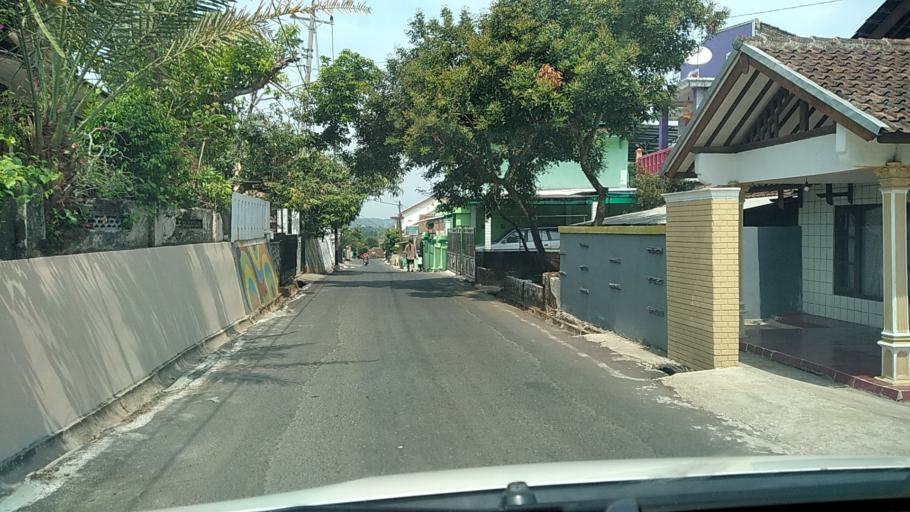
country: ID
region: Central Java
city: Ungaran
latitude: -7.0776
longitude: 110.3181
